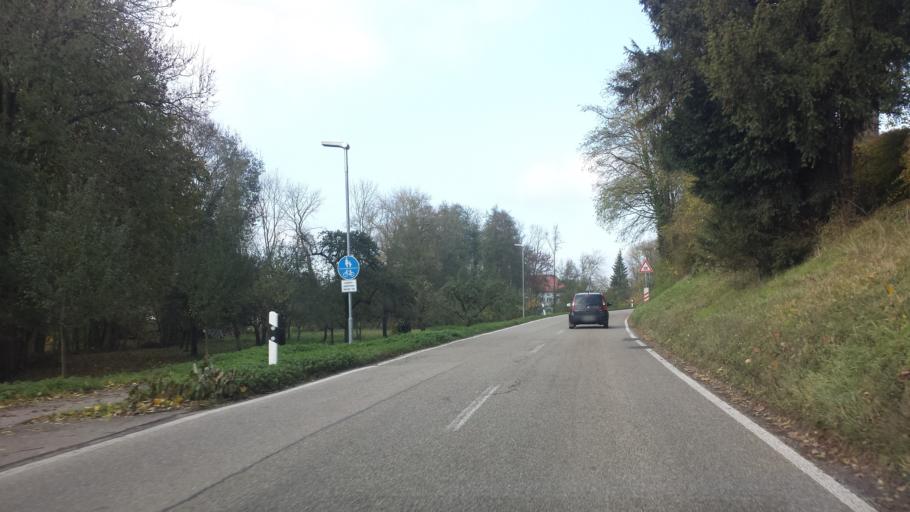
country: DE
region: Baden-Wuerttemberg
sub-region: Karlsruhe Region
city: Zaisenhausen
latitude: 49.1069
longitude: 8.7461
